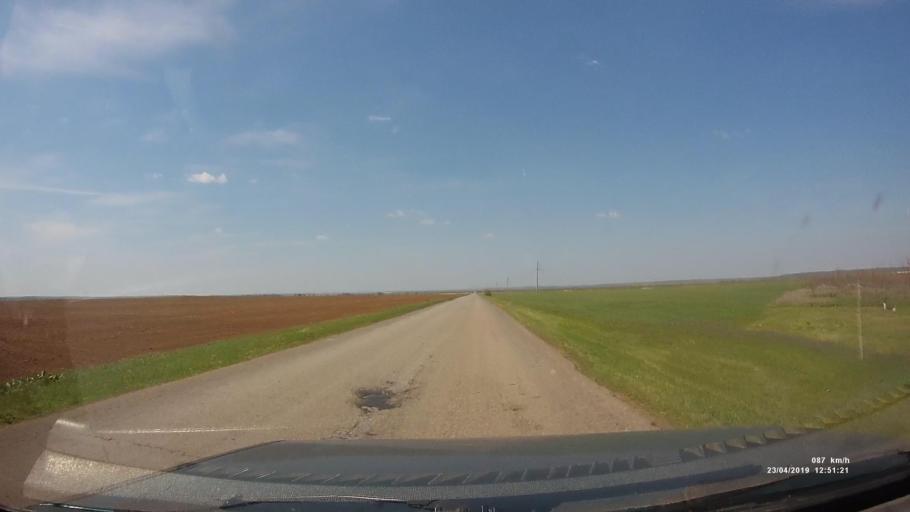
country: RU
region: Kalmykiya
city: Yashalta
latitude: 46.5539
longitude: 42.6241
